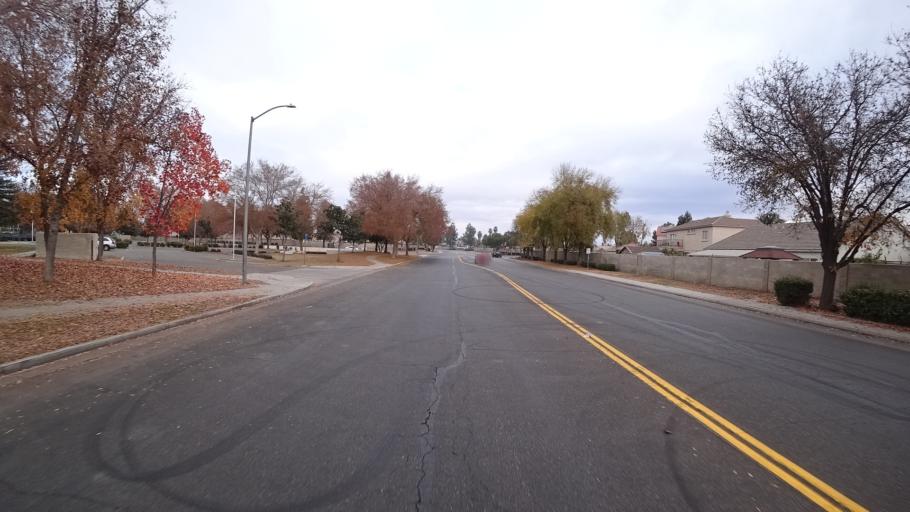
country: US
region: California
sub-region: Kern County
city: Greenfield
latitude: 35.3031
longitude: -119.0804
